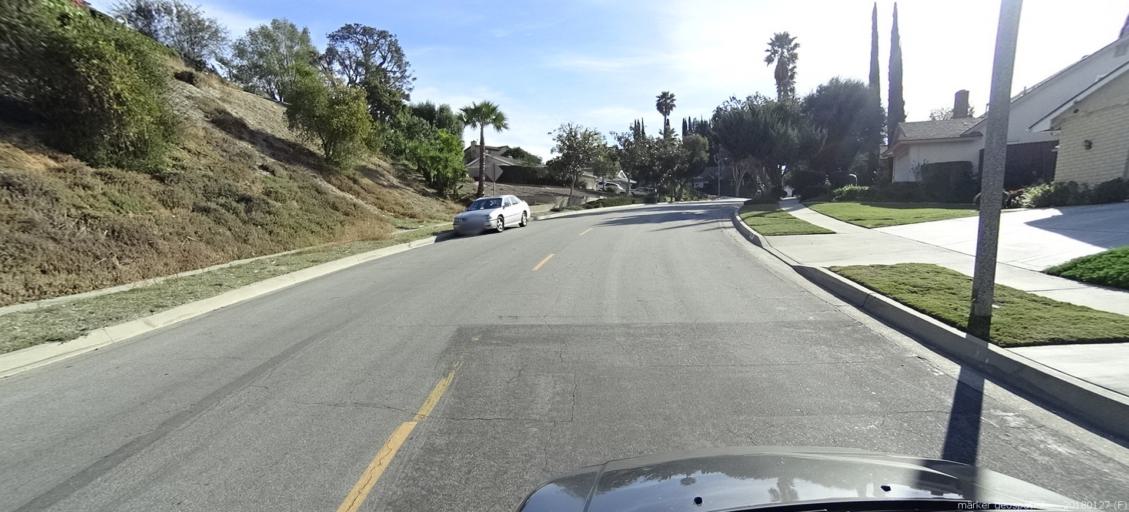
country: US
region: California
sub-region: Los Angeles County
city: Diamond Bar
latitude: 34.0312
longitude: -117.8035
